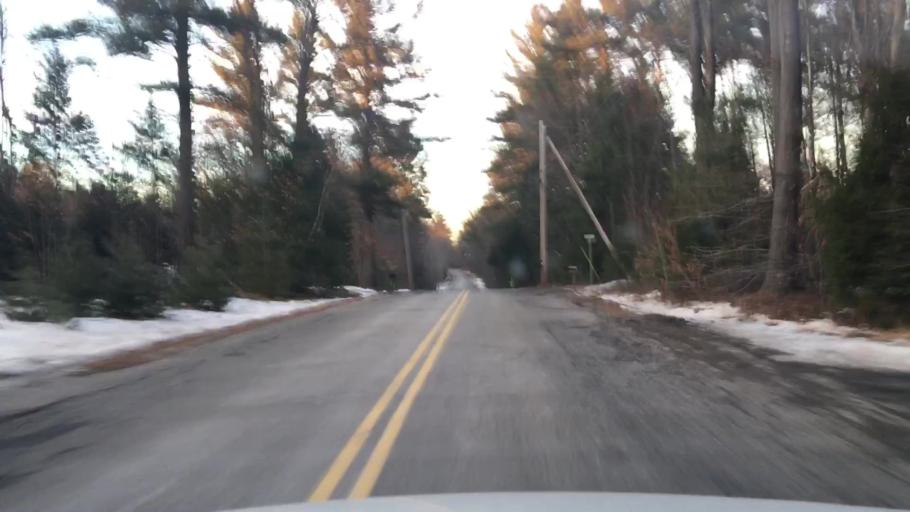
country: US
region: Maine
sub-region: York County
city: Berwick
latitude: 43.3300
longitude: -70.8643
